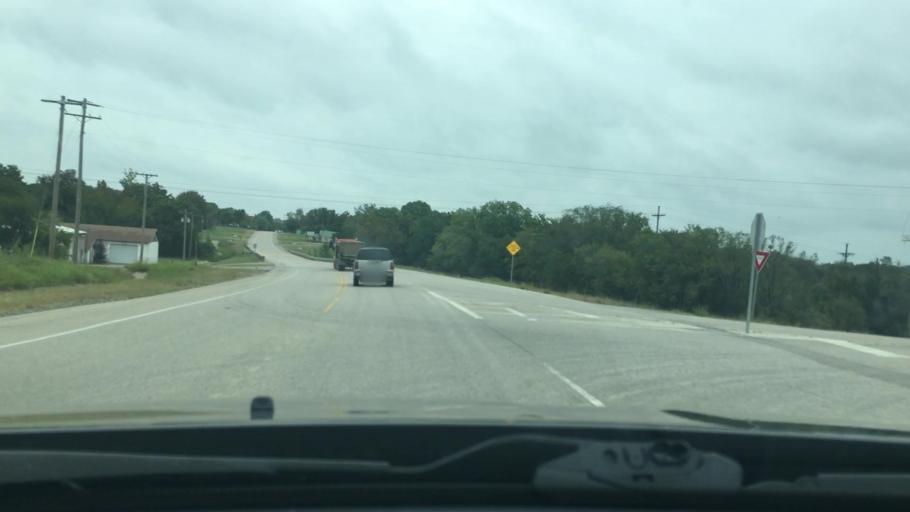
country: US
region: Oklahoma
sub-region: Pontotoc County
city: Ada
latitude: 34.6078
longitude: -96.6336
